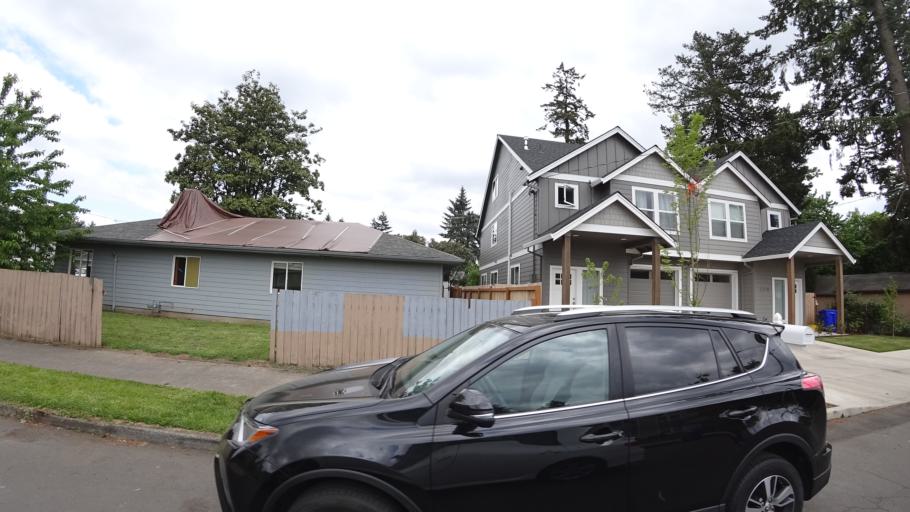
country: US
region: Oregon
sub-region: Multnomah County
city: Lents
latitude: 45.5061
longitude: -122.5390
